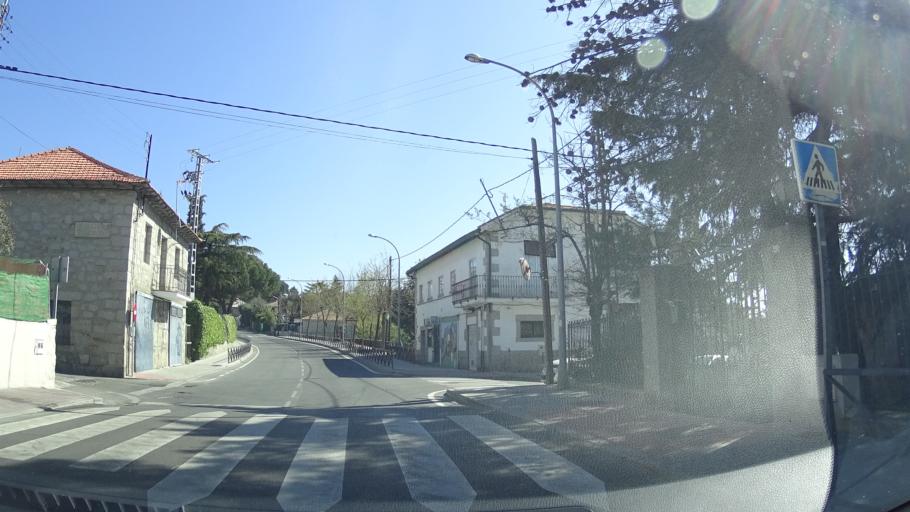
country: ES
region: Madrid
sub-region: Provincia de Madrid
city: Hoyo de Manzanares
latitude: 40.6215
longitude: -3.9049
